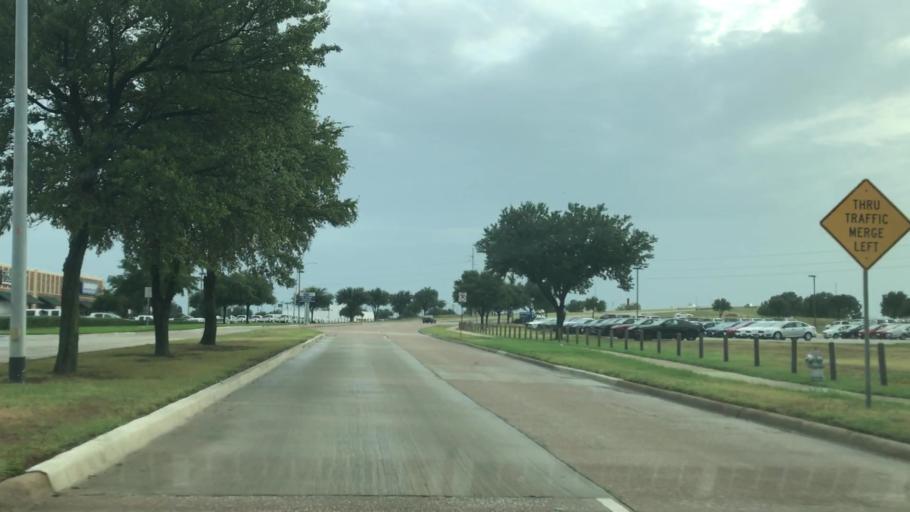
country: US
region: Texas
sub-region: Denton County
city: Lewisville
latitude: 33.0571
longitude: -97.0069
